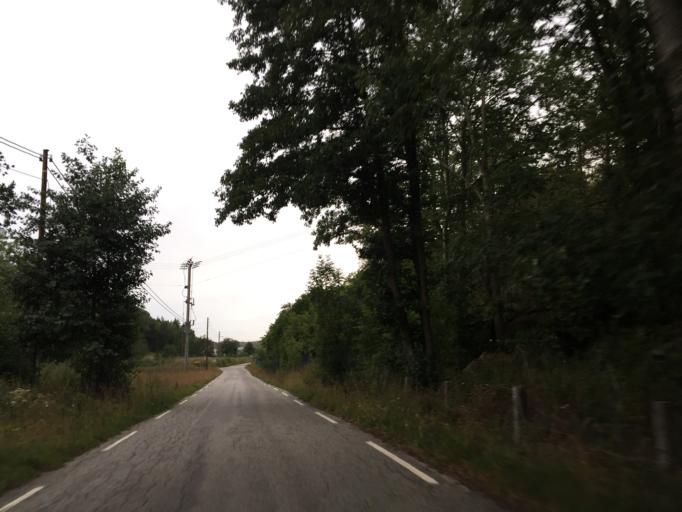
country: NO
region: Ostfold
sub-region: Hvaler
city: Skjaerhalden
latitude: 59.0762
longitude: 11.0064
